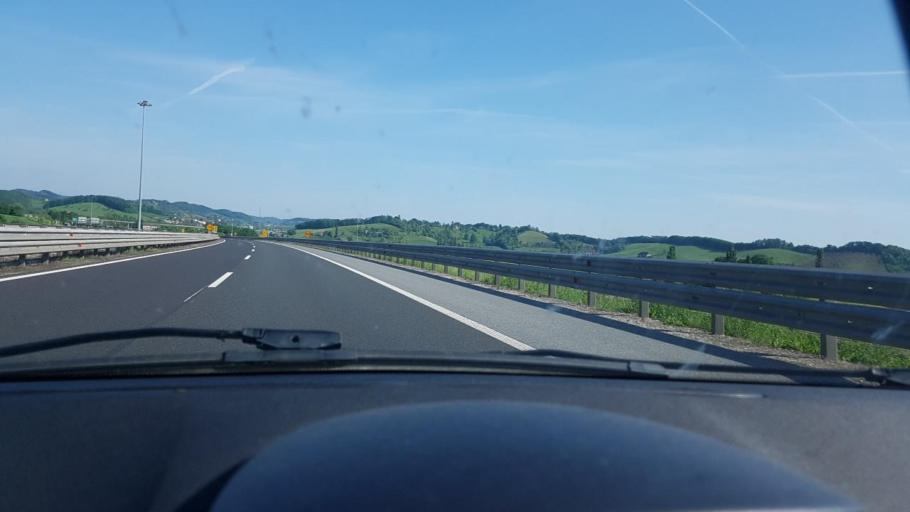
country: SI
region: Pesnica
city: Pesnica pri Mariboru
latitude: 46.5832
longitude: 15.6908
